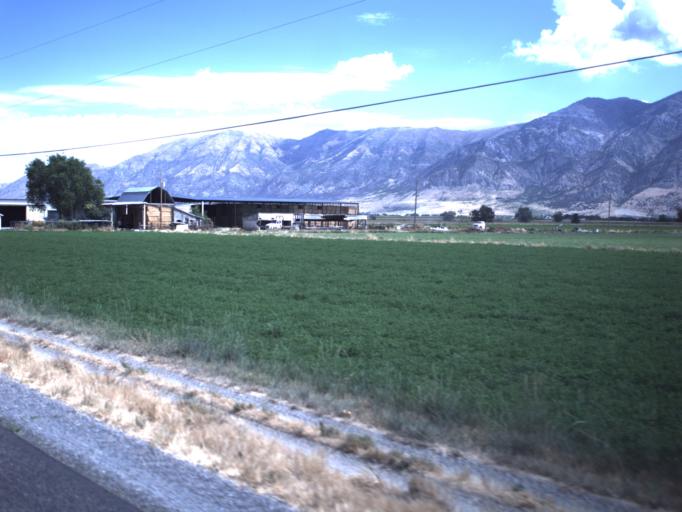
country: US
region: Utah
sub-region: Box Elder County
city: Honeyville
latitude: 41.5825
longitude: -112.1297
